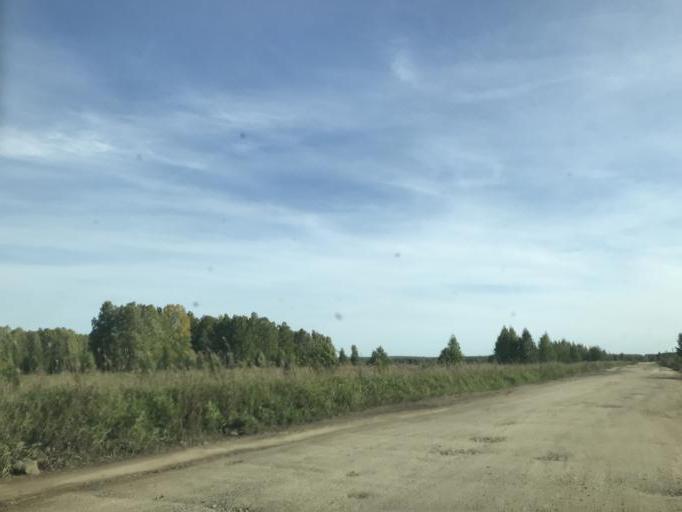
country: RU
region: Chelyabinsk
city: Poletayevo
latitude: 54.9801
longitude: 60.9685
